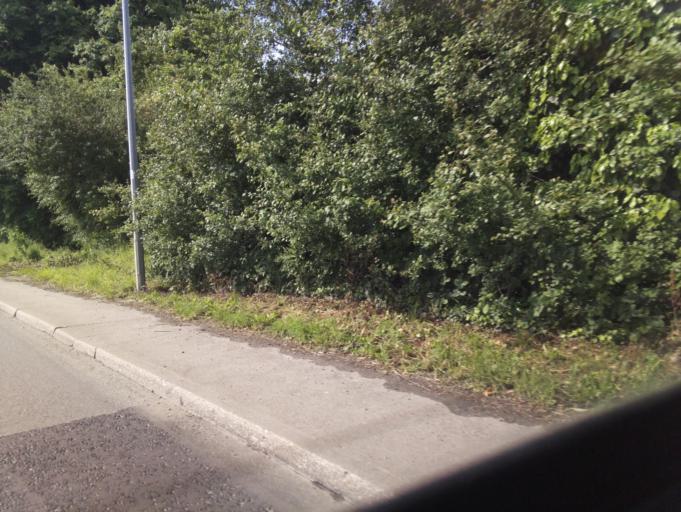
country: GB
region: England
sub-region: Lincolnshire
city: Skellingthorpe
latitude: 53.1558
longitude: -0.6288
